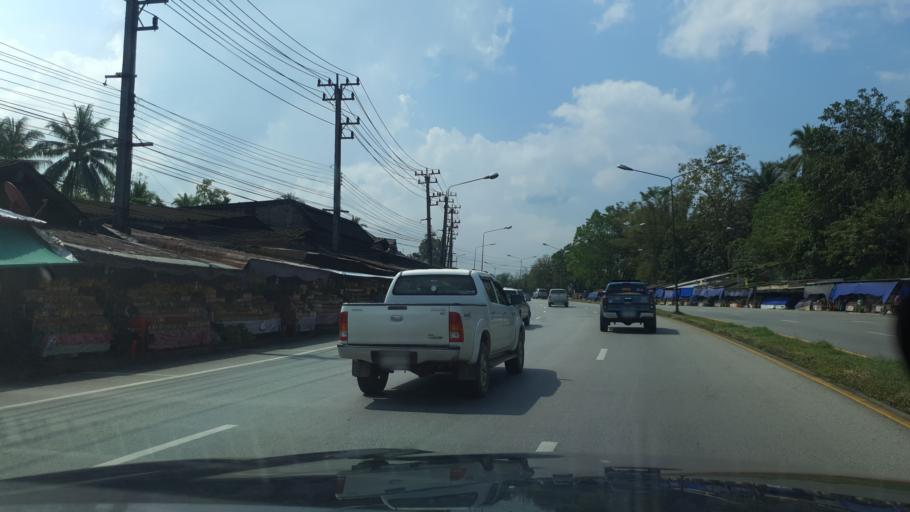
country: TH
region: Chumphon
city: Pathio
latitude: 10.8504
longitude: 99.2320
